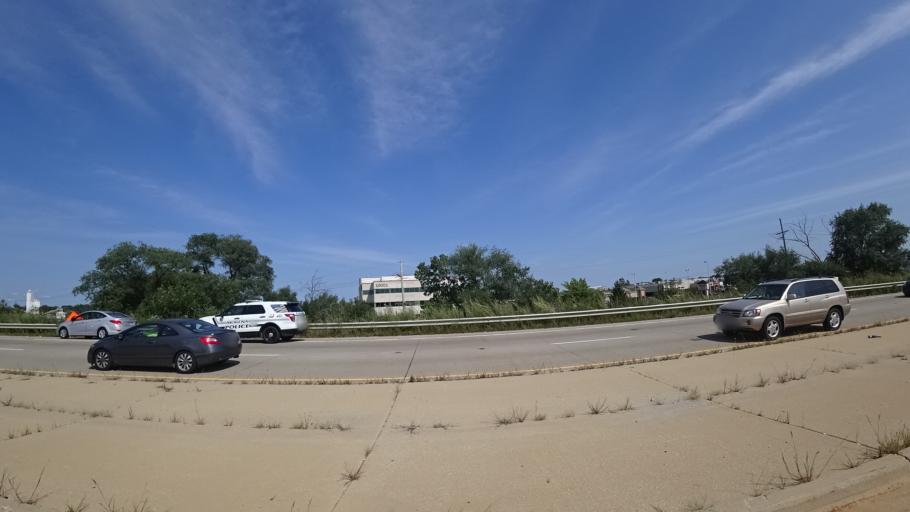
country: US
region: Illinois
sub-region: Cook County
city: Orland Hills
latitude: 41.5451
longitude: -87.8511
